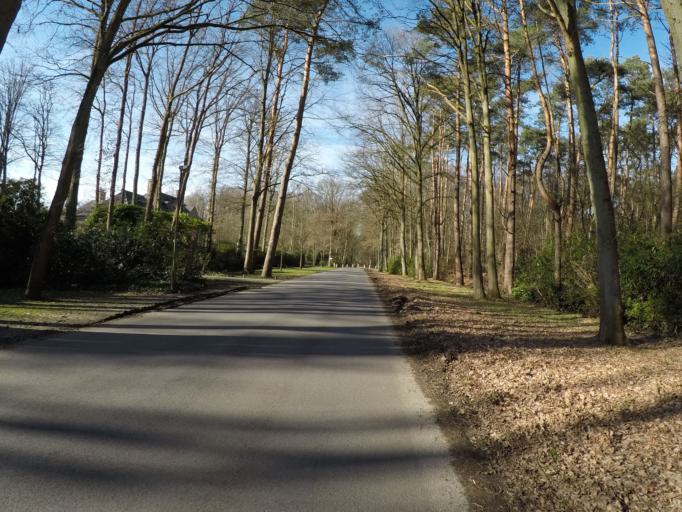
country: BE
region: Flanders
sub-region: Provincie Antwerpen
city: Schilde
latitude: 51.2446
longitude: 4.5522
